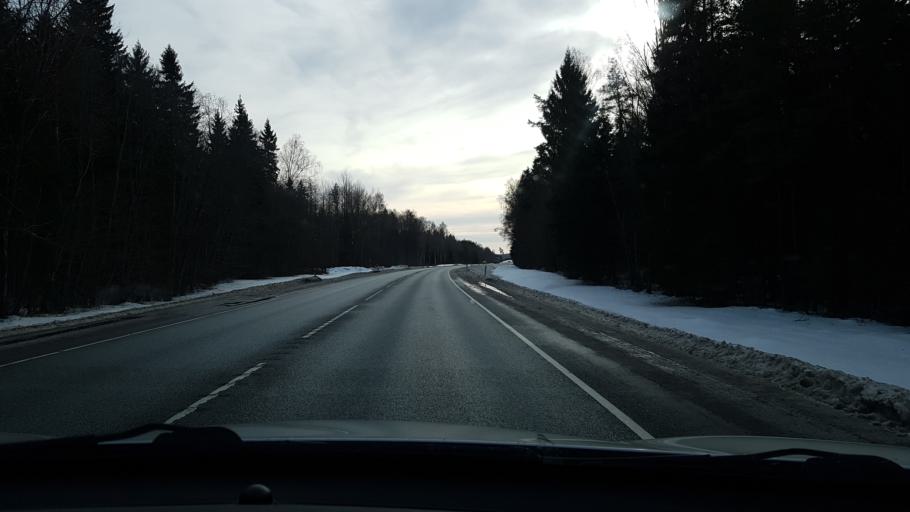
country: EE
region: Jaervamaa
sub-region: Paide linn
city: Paide
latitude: 59.0769
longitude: 25.4229
